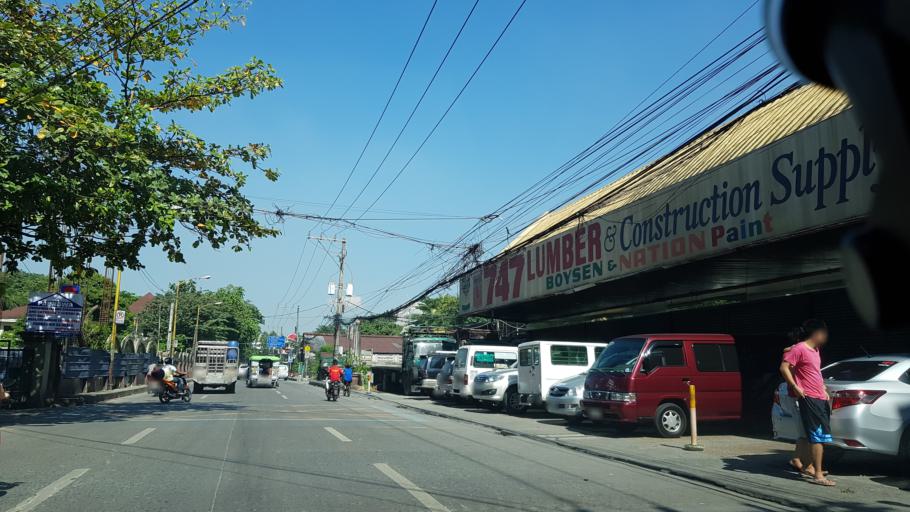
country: PH
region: Calabarzon
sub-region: Province of Rizal
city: Pateros
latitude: 14.5600
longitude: 121.0828
